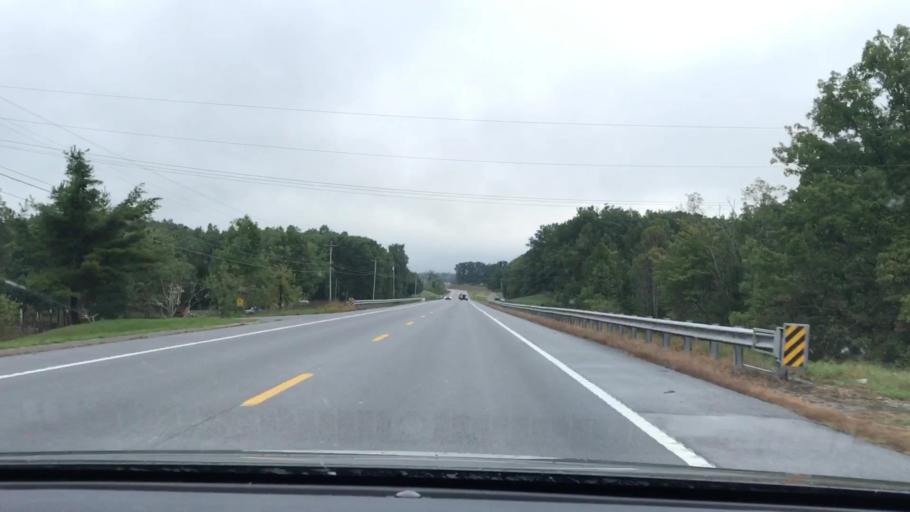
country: US
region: Tennessee
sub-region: Fentress County
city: Grimsley
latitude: 36.2941
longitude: -84.9751
